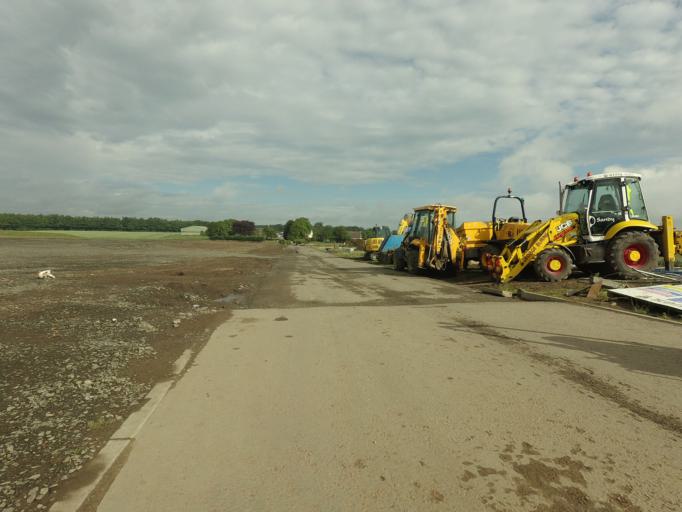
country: GB
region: Scotland
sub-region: West Lothian
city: East Calder
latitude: 55.9047
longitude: -3.4464
